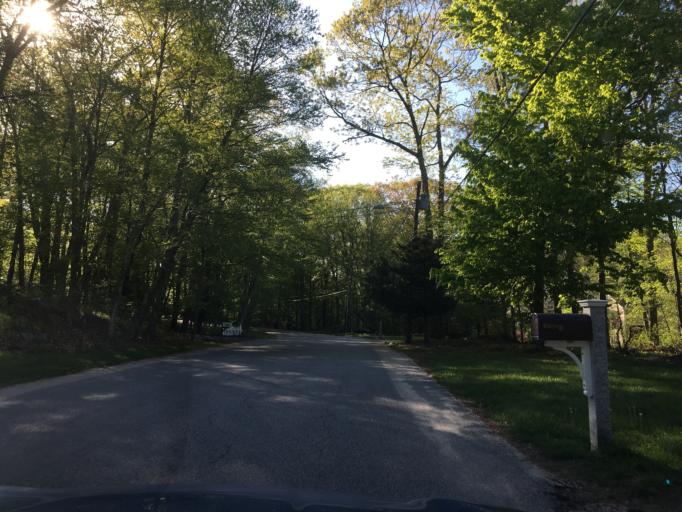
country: US
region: Rhode Island
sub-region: Washington County
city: Exeter
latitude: 41.6097
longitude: -71.5166
